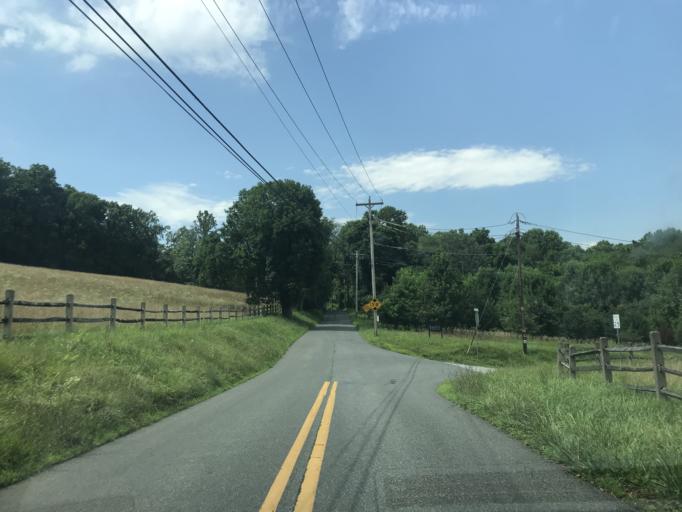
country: US
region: Delaware
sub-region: New Castle County
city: Greenville
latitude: 39.7807
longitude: -75.6426
